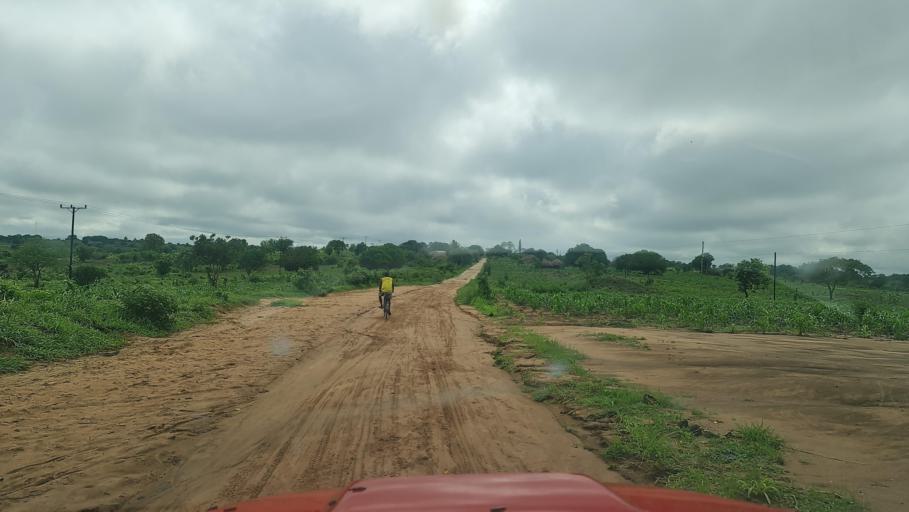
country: MW
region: Southern Region
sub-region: Nsanje District
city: Nsanje
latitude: -17.2028
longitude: 35.6875
